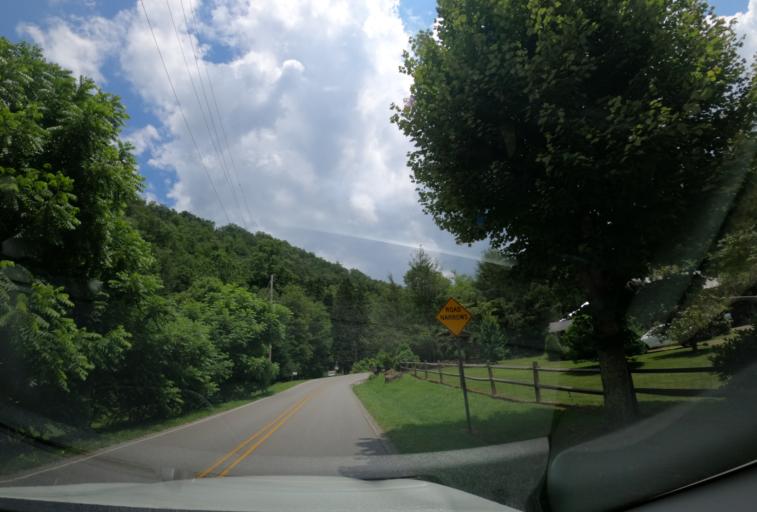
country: US
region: North Carolina
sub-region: Haywood County
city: Waynesville
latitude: 35.4275
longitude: -82.9176
